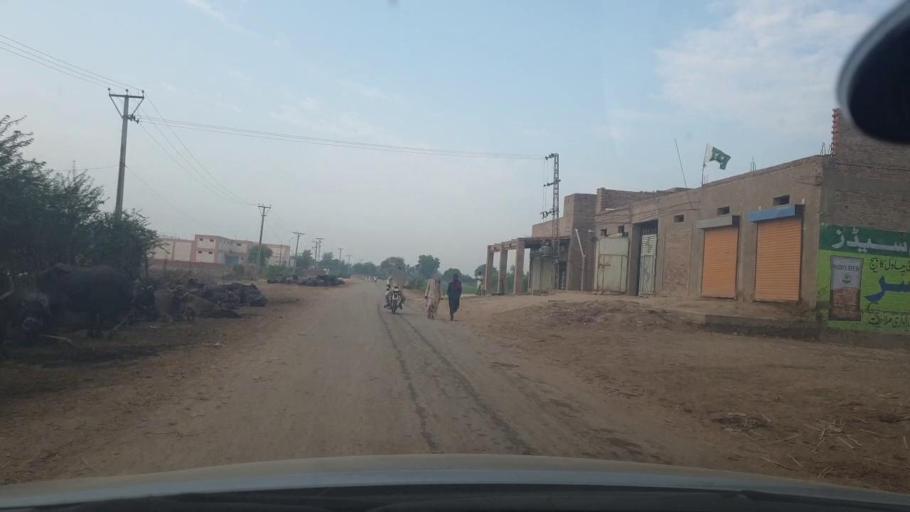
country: PK
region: Sindh
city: Jacobabad
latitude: 28.2767
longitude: 68.4235
